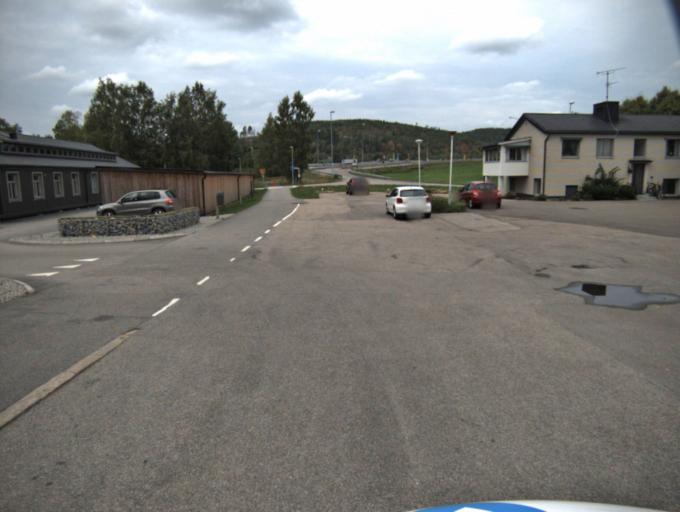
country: SE
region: Vaestra Goetaland
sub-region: Ulricehamns Kommun
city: Ulricehamn
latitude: 57.8022
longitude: 13.4112
